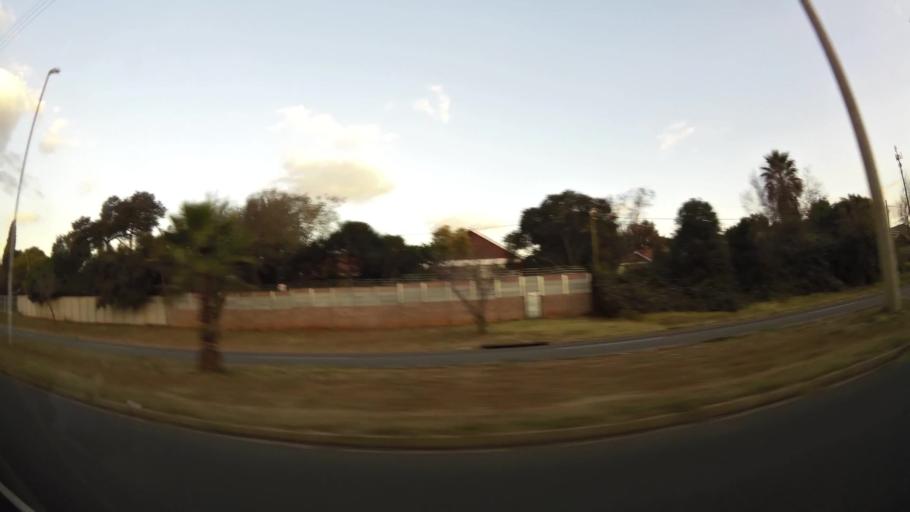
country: ZA
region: Gauteng
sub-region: West Rand District Municipality
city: Krugersdorp
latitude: -26.0768
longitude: 27.7810
